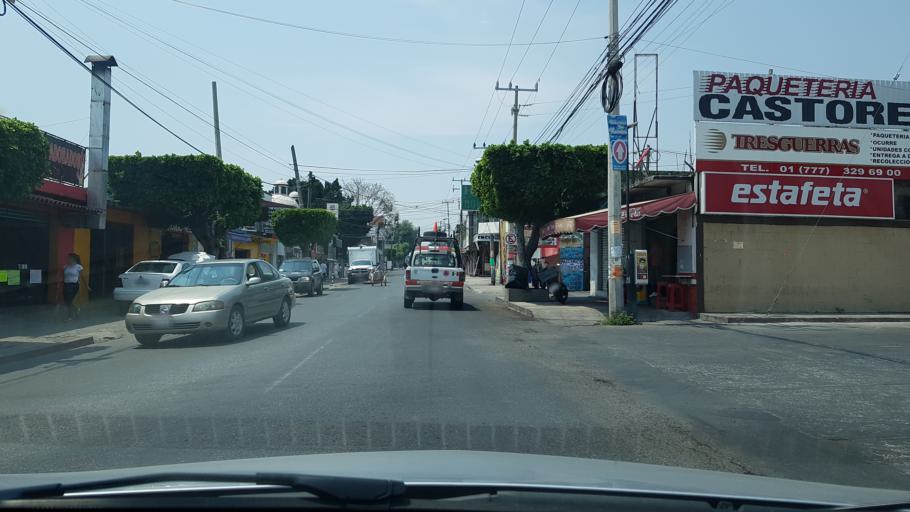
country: MX
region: Morelos
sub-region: Jiutepec
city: Jiutepec
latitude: 18.8965
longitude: -99.1697
